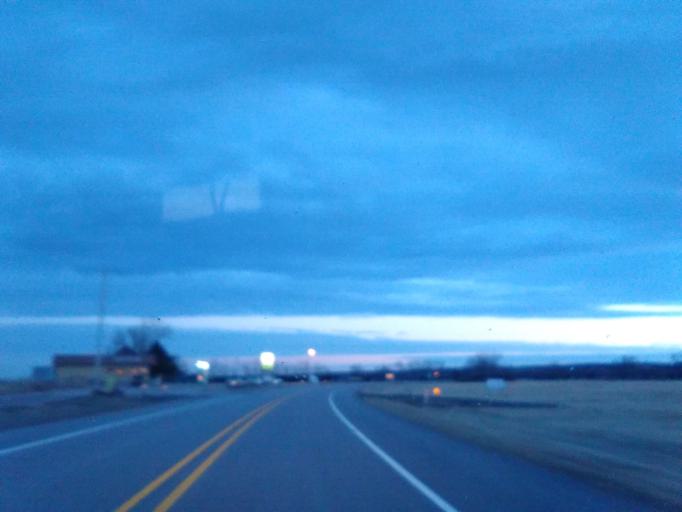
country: US
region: Nebraska
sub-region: Garden County
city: Oshkosh
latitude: 41.3269
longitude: -102.1303
